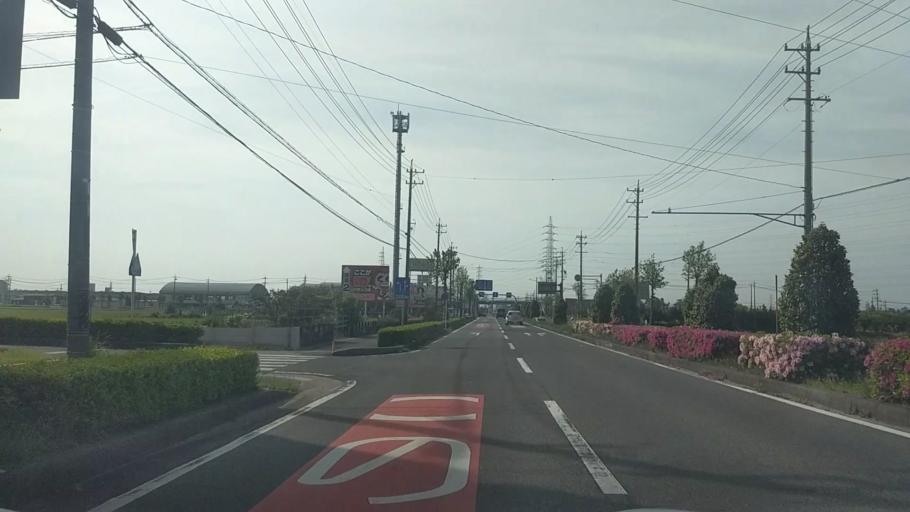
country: JP
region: Aichi
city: Anjo
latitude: 34.9625
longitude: 137.0612
